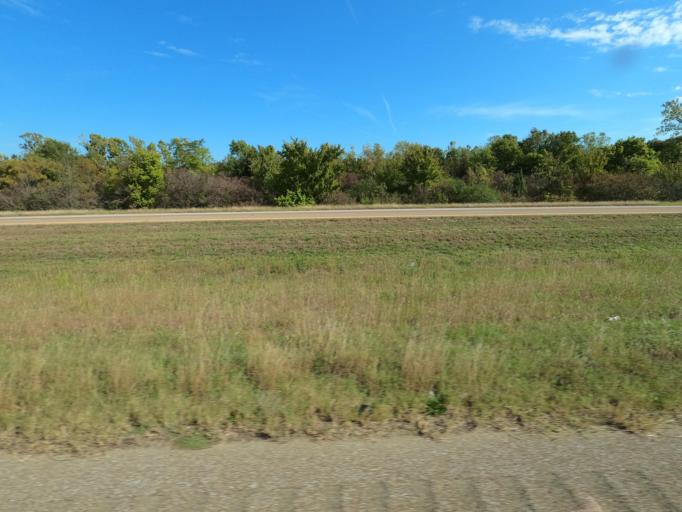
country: US
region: Tennessee
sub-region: Shelby County
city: Millington
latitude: 35.3275
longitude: -89.8891
